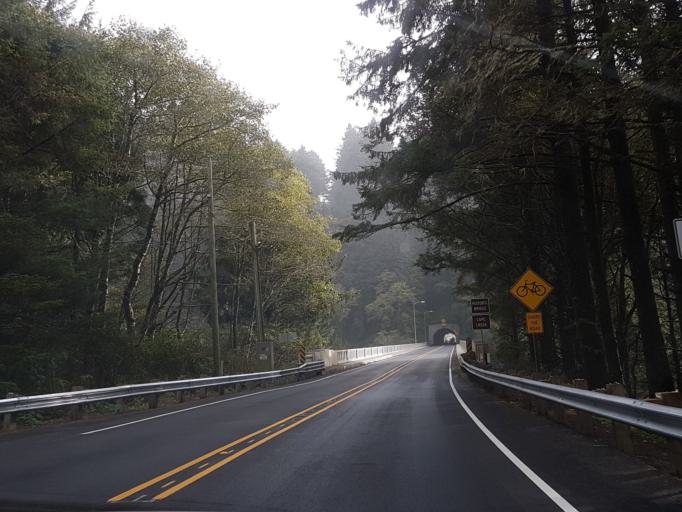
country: US
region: Oregon
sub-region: Lane County
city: Florence
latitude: 44.1349
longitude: -124.1216
